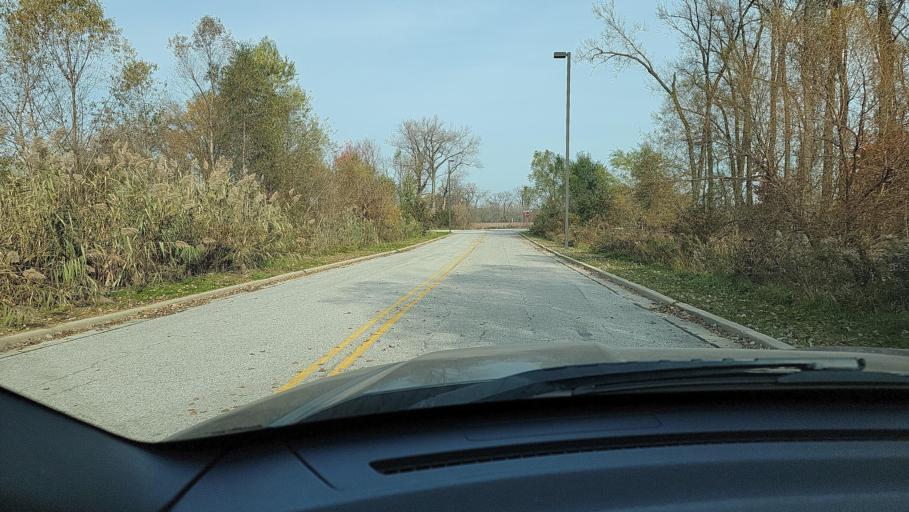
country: US
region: Indiana
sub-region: Porter County
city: Ogden Dunes
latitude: 41.6048
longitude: -87.1786
